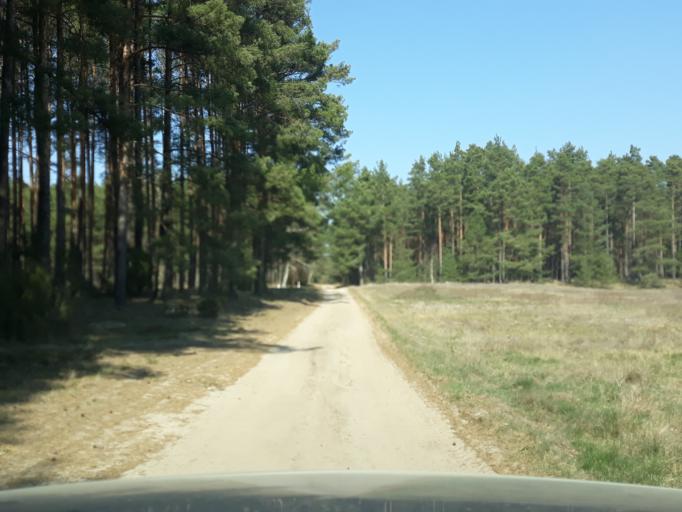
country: PL
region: Pomeranian Voivodeship
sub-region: Powiat bytowski
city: Lipnica
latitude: 53.8505
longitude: 17.4305
